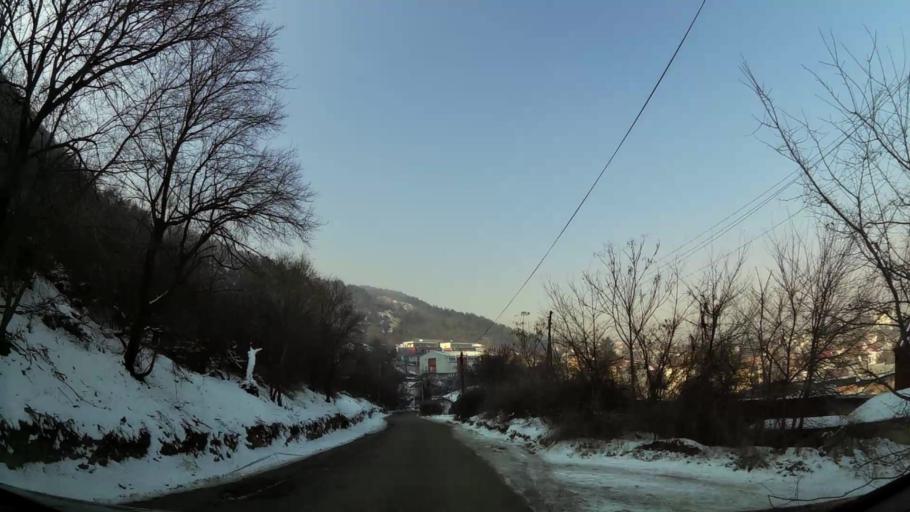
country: MK
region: Sopiste
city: Sopishte
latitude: 41.9718
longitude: 21.4363
